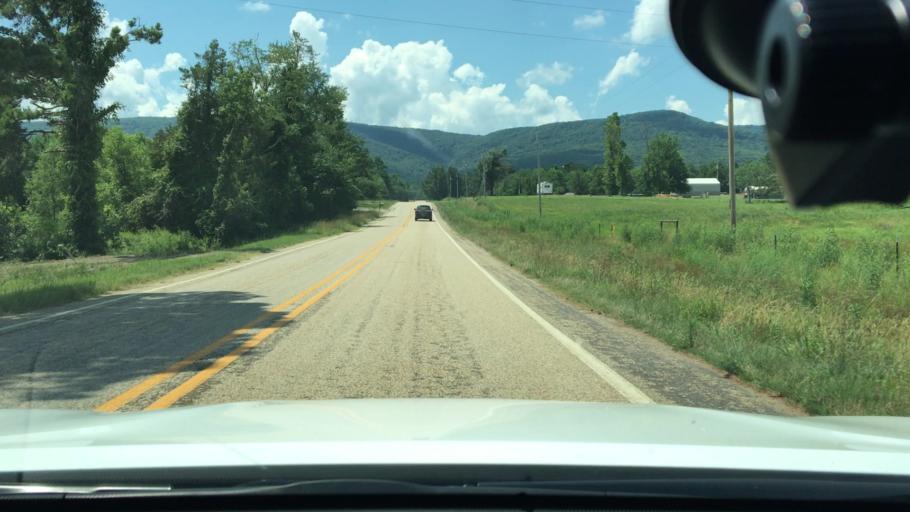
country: US
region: Arkansas
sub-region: Logan County
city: Paris
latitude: 35.2055
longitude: -93.6347
